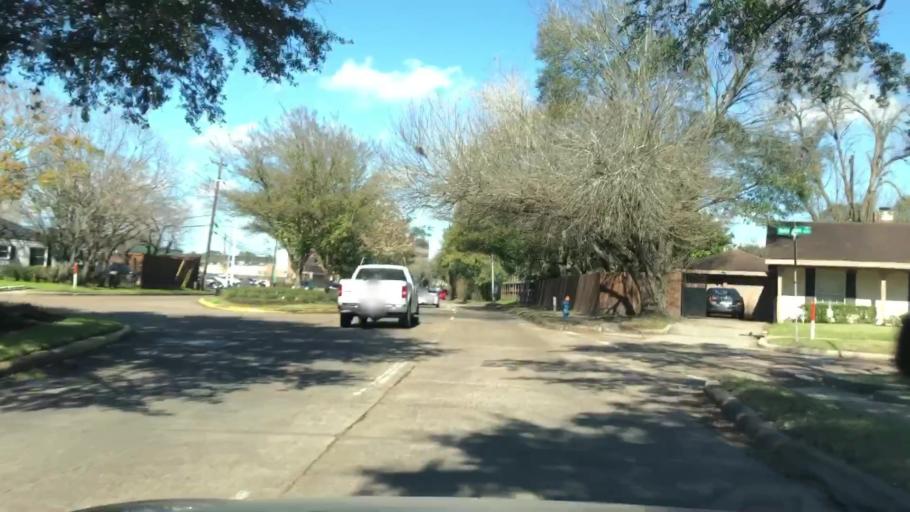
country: US
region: Texas
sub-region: Harris County
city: Bellaire
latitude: 29.6725
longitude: -95.4925
